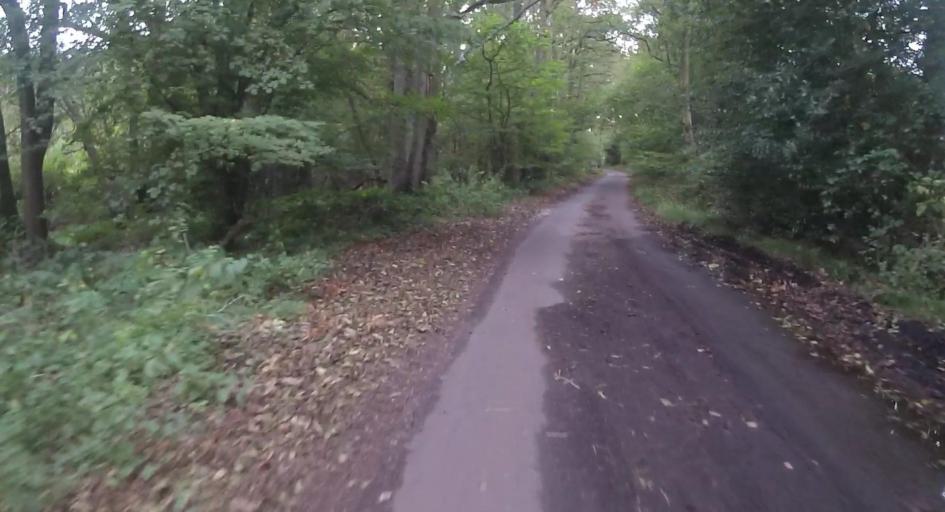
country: GB
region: England
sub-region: Hampshire
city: Hook
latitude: 51.3134
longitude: -0.9291
